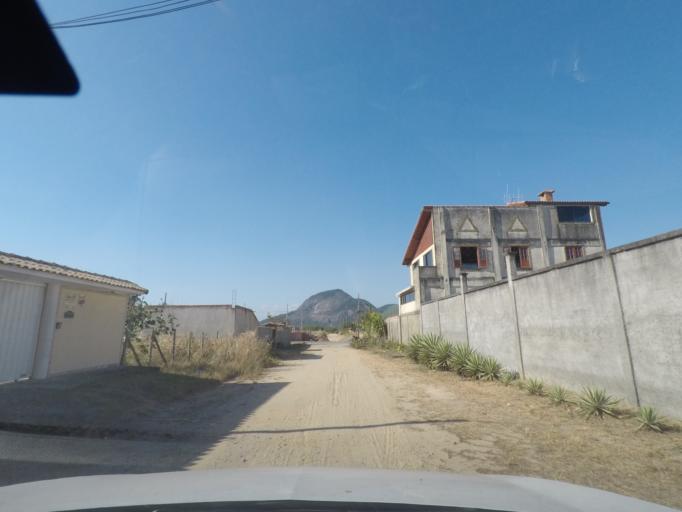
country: BR
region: Rio de Janeiro
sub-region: Marica
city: Marica
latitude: -22.9675
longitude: -42.9118
